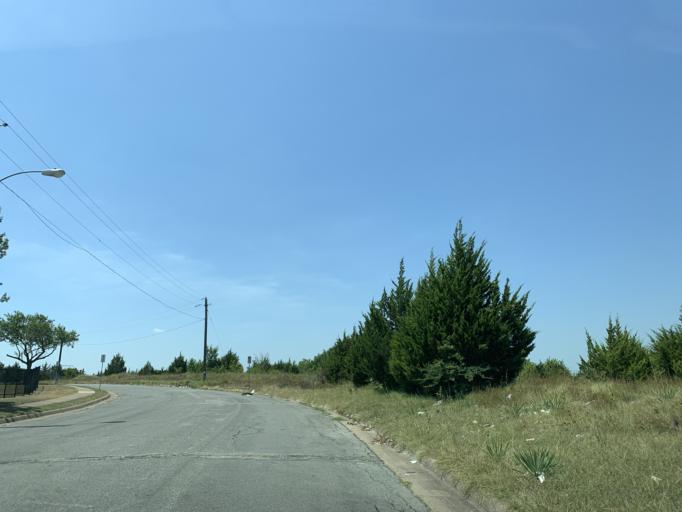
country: US
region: Texas
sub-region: Dallas County
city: Hutchins
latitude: 32.6751
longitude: -96.7666
